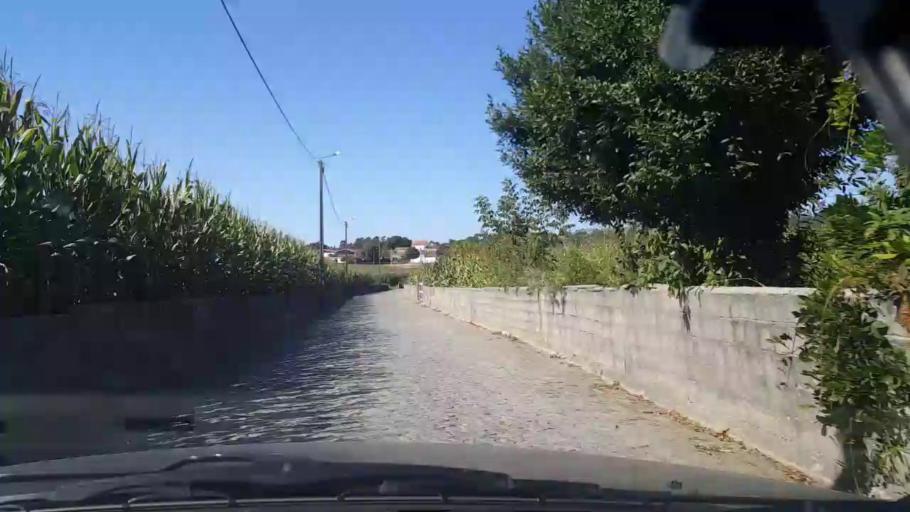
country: PT
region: Braga
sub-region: Vila Nova de Famalicao
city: Ribeirao
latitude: 41.3578
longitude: -8.6347
